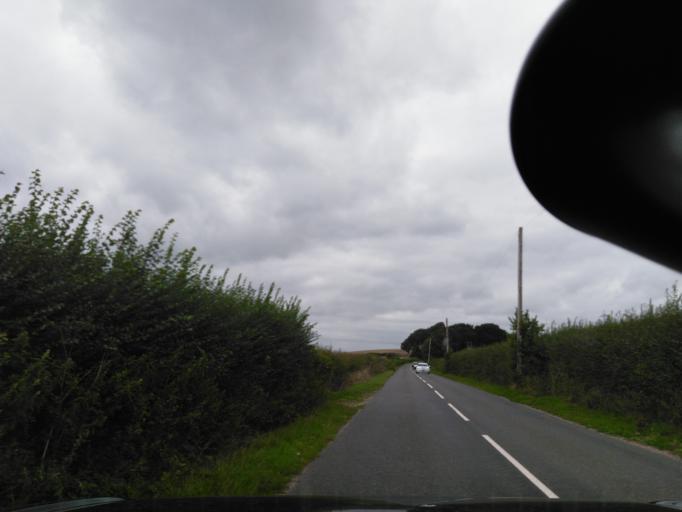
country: GB
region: England
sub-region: Dorset
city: Lytchett Matravers
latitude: 50.7356
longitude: -2.1185
